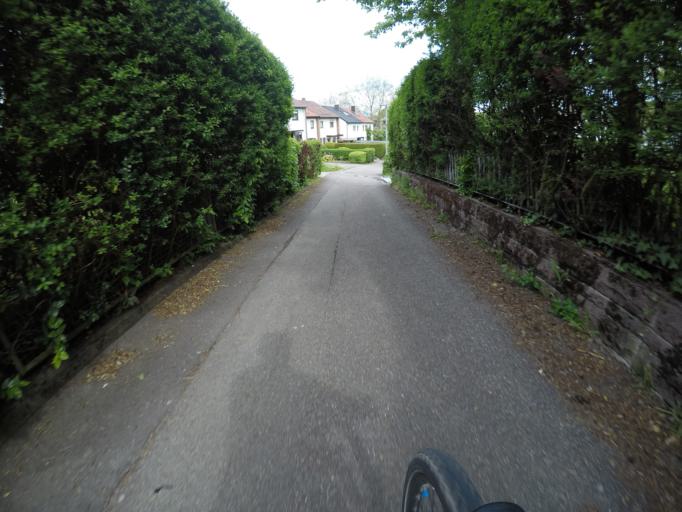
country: DE
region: Baden-Wuerttemberg
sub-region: Regierungsbezirk Stuttgart
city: Boeblingen
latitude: 48.6788
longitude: 9.0018
